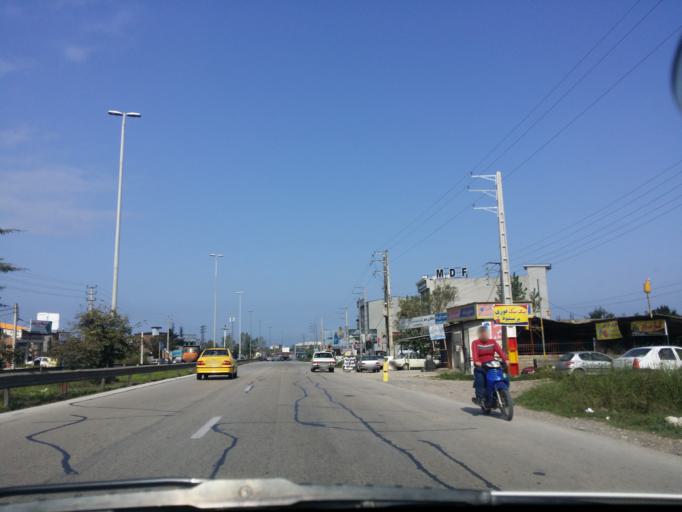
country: IR
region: Mazandaran
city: Chalus
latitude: 36.6677
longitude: 51.3967
